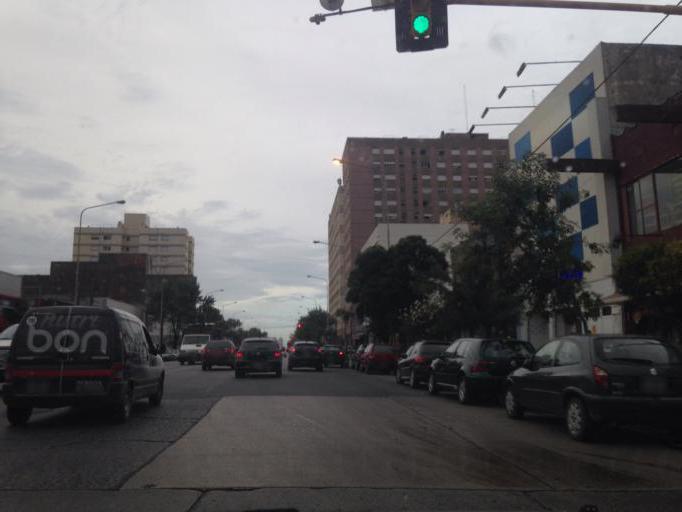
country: AR
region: Buenos Aires
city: Mar del Plata
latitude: -38.0189
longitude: -57.5711
